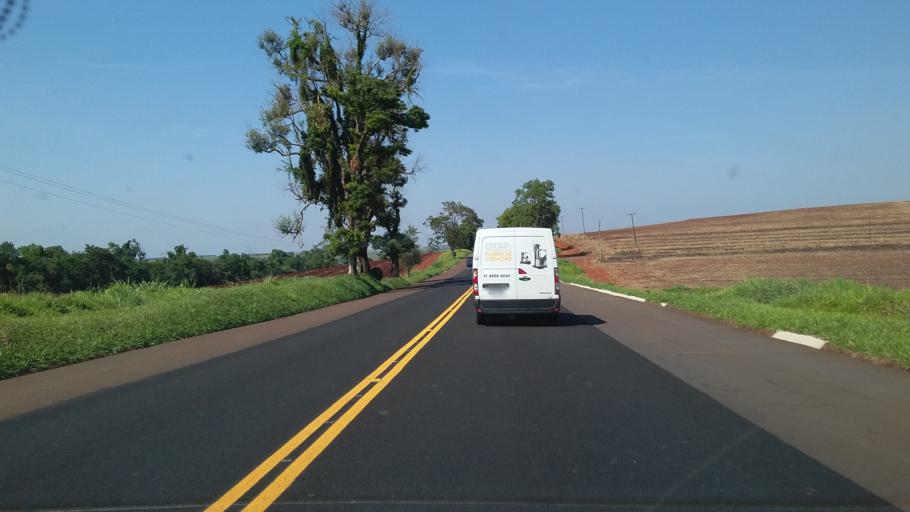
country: BR
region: Parana
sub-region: Bandeirantes
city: Bandeirantes
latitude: -23.1335
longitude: -50.4752
